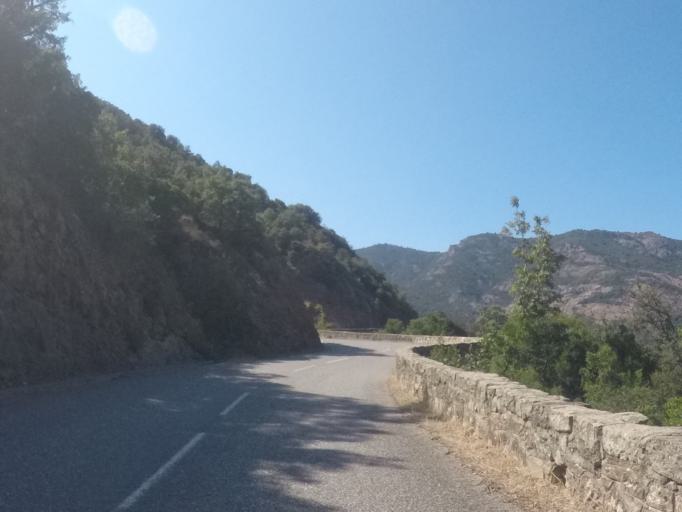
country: FR
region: Corsica
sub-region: Departement de la Haute-Corse
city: Calvi
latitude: 42.3683
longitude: 8.6712
